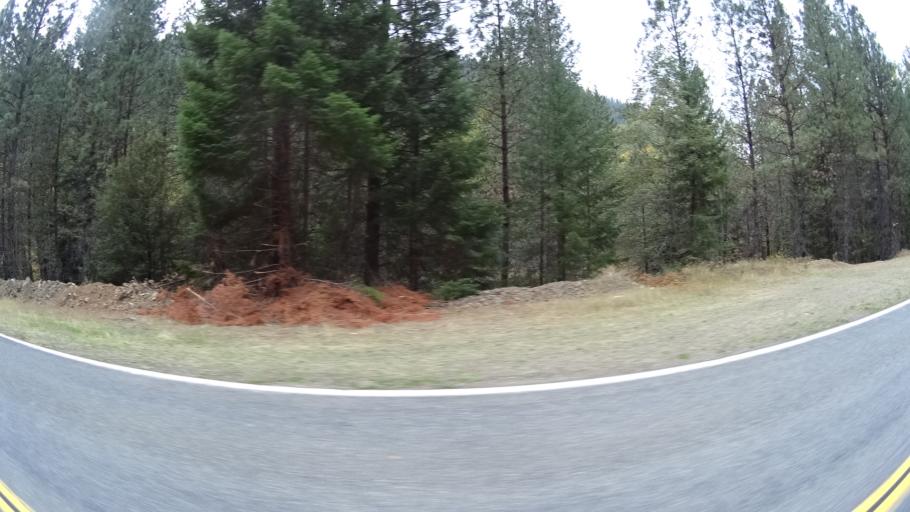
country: US
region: California
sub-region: Siskiyou County
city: Happy Camp
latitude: 41.8930
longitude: -123.4337
